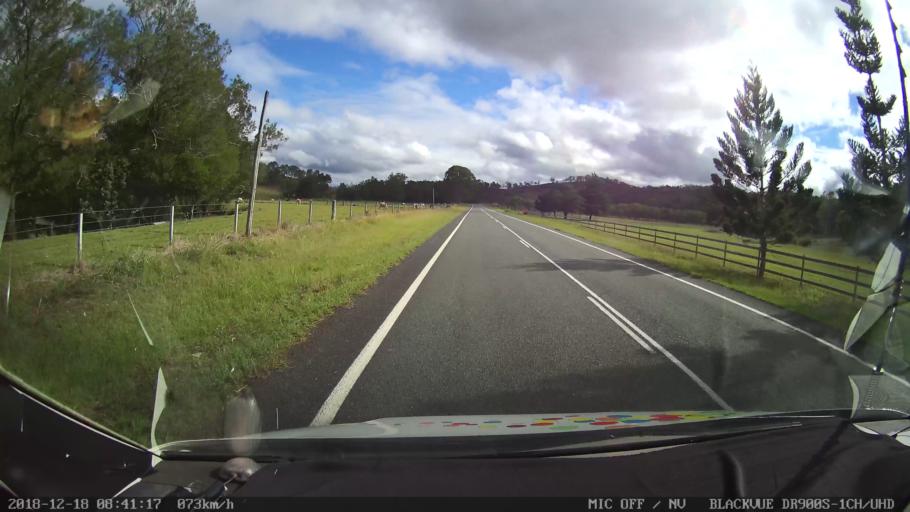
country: AU
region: Queensland
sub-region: Logan
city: Cedar Vale
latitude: -28.2379
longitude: 152.8560
